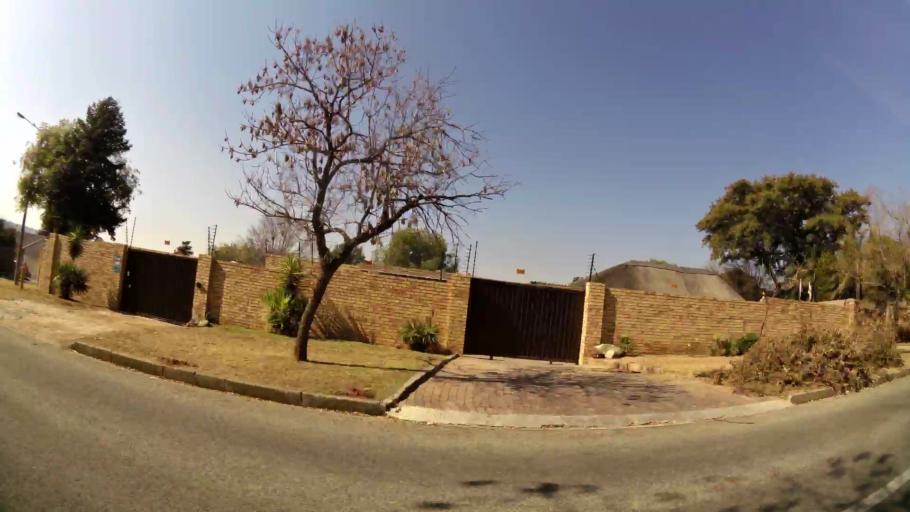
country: ZA
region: Gauteng
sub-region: City of Johannesburg Metropolitan Municipality
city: Modderfontein
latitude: -26.1110
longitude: 28.1661
